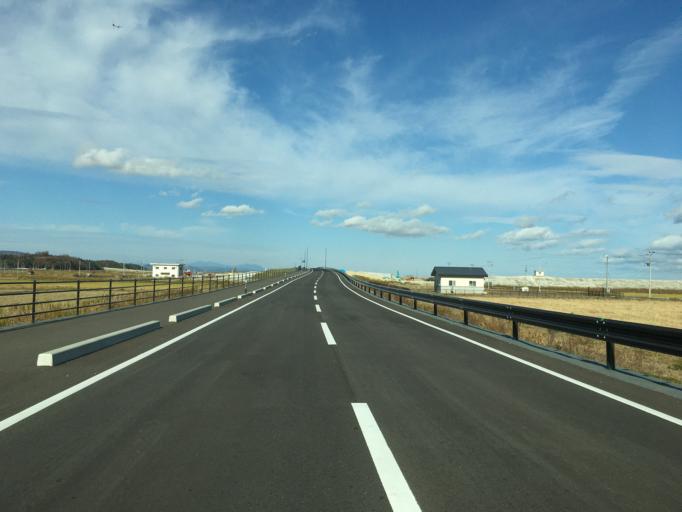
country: JP
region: Miyagi
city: Watari
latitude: 37.9223
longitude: 140.9145
